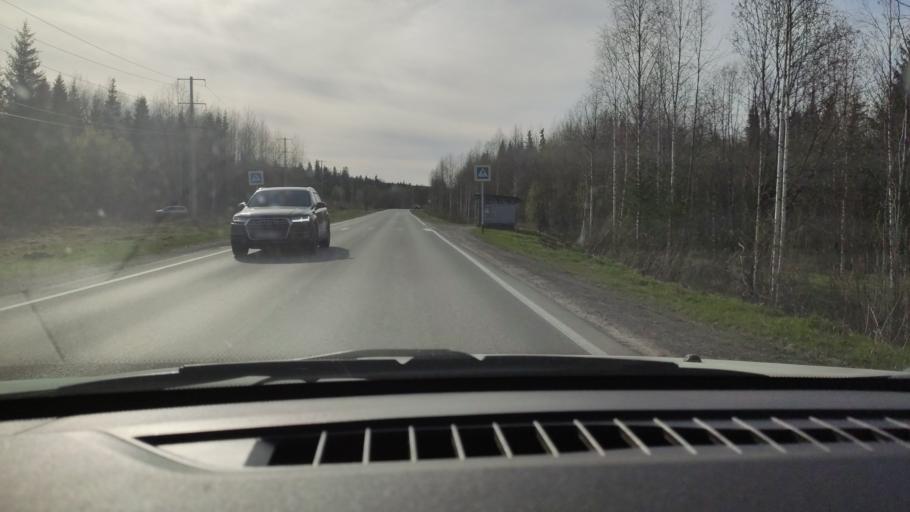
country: RU
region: Perm
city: Novyye Lyady
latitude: 57.9582
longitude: 56.5538
